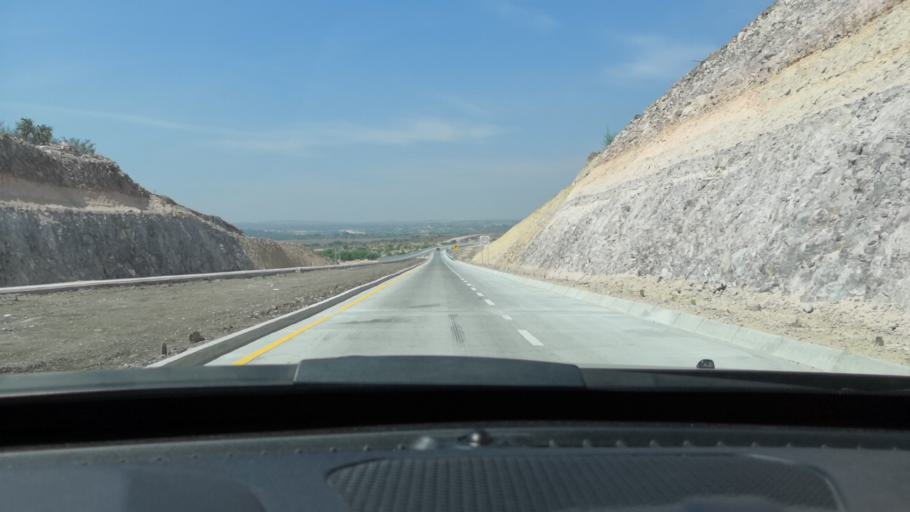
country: MX
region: Guanajuato
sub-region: Purisima del Rincon
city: Potrerillos (Guanajal)
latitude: 21.0847
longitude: -101.8317
